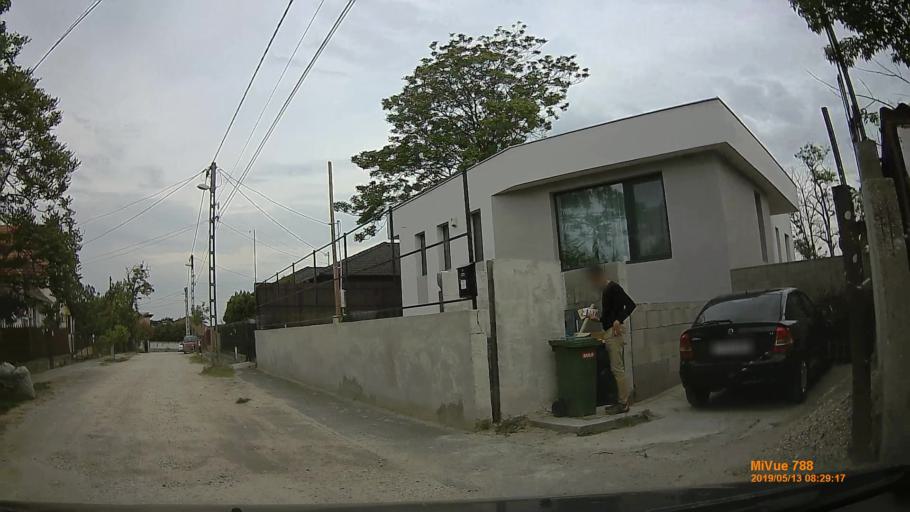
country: HU
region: Budapest
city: Budapest XXIII. keruelet
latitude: 47.4065
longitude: 19.0963
